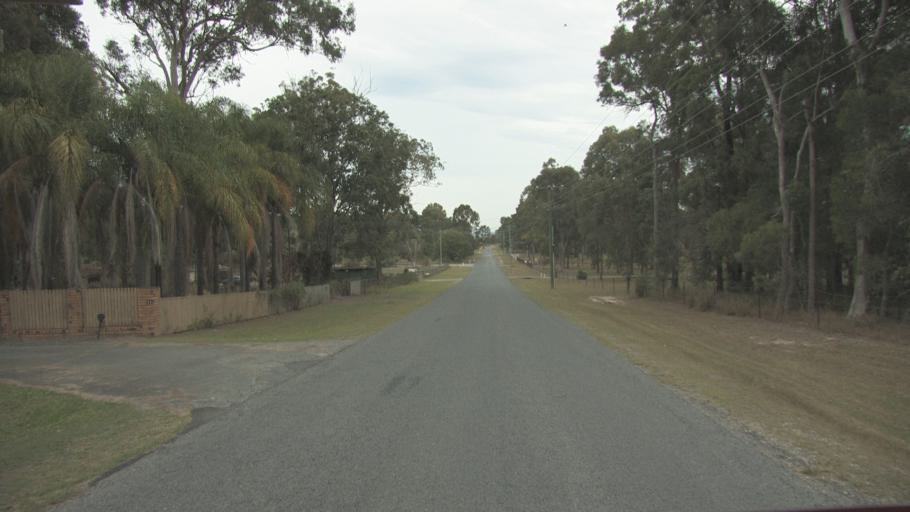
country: AU
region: Queensland
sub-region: Logan
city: Chambers Flat
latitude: -27.7991
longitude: 153.1227
